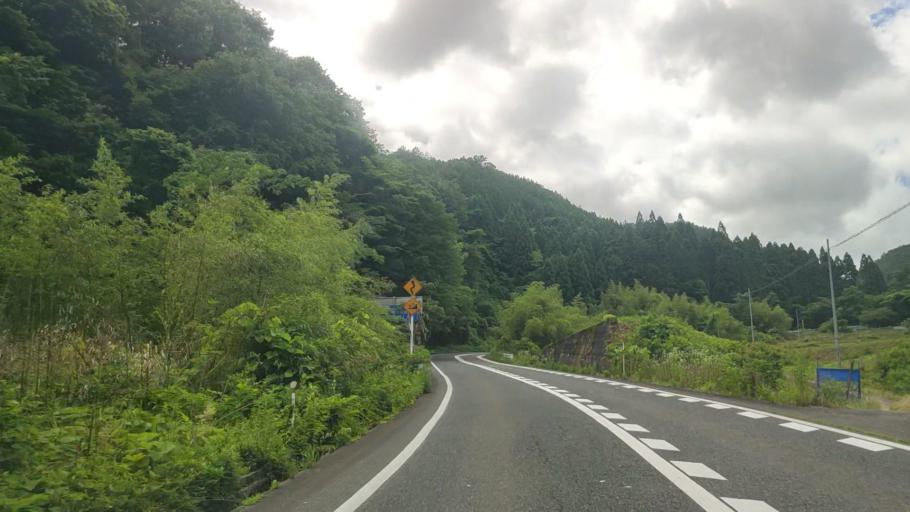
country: JP
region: Tottori
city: Yonago
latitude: 35.2777
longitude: 133.4310
